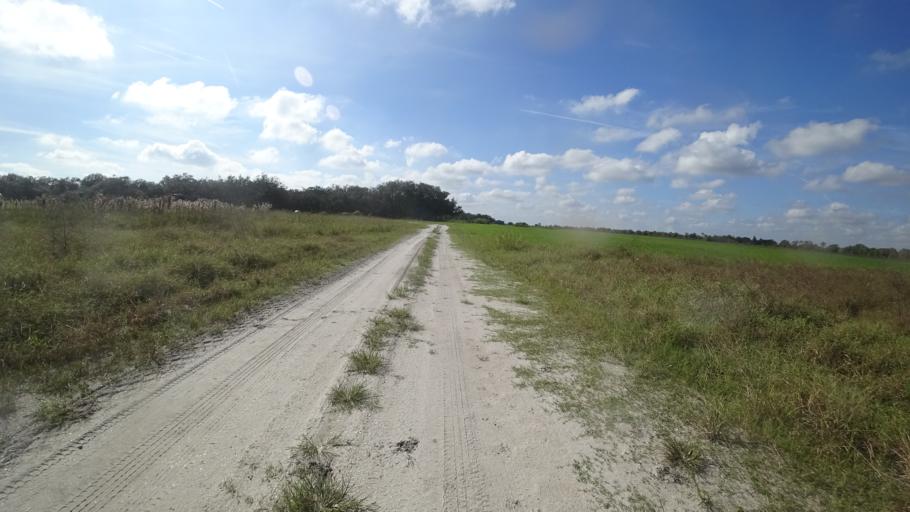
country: US
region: Florida
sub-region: Sarasota County
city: Lake Sarasota
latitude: 27.3724
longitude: -82.1612
